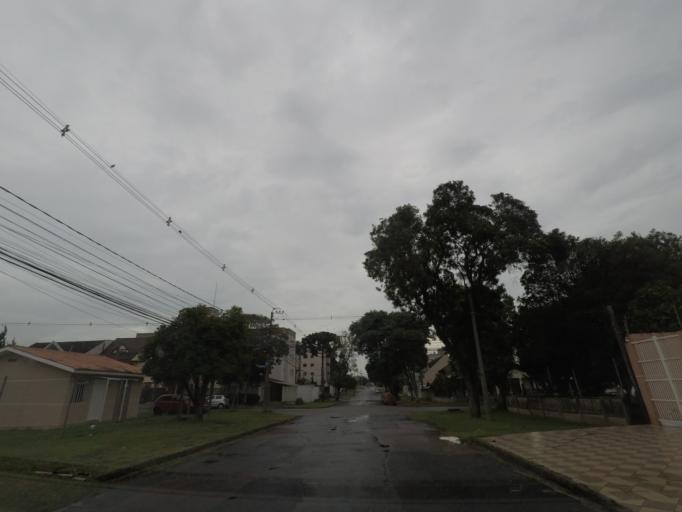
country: BR
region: Parana
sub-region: Curitiba
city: Curitiba
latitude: -25.4759
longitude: -49.3123
